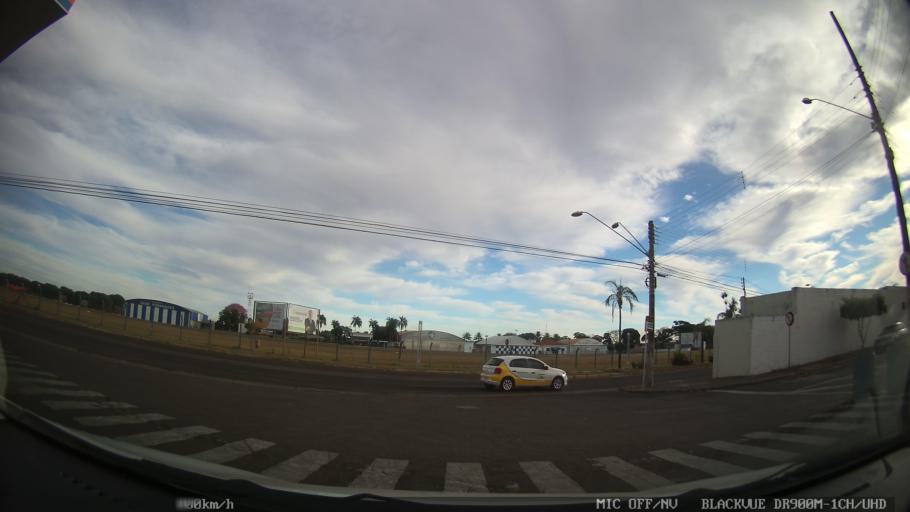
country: BR
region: Sao Paulo
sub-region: Catanduva
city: Catanduva
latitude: -21.1467
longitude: -48.9851
